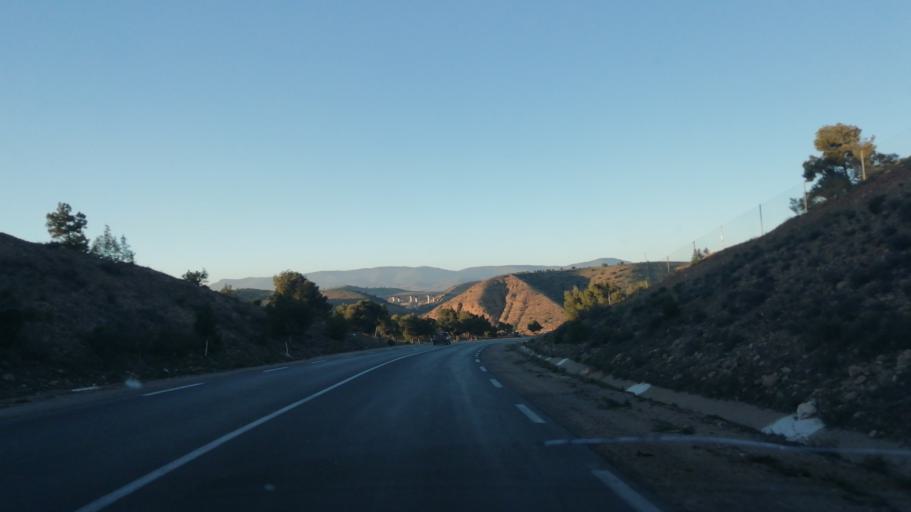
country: DZ
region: Tlemcen
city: Nedroma
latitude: 34.8817
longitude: -1.6703
